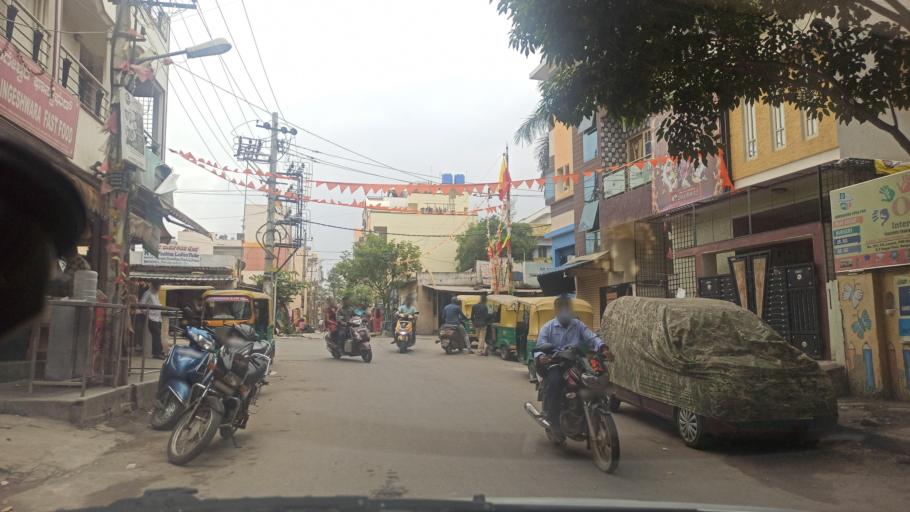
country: IN
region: Karnataka
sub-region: Bangalore Urban
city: Bangalore
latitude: 13.0354
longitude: 77.6014
